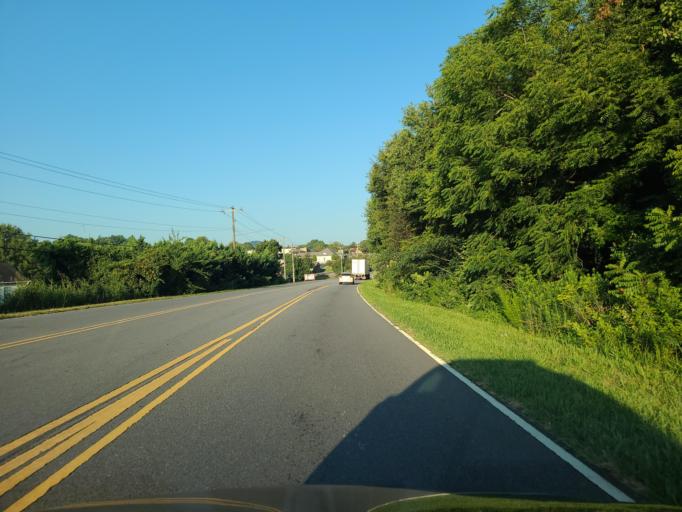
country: US
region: North Carolina
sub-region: Catawba County
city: Mountain View
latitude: 35.6884
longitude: -81.3621
